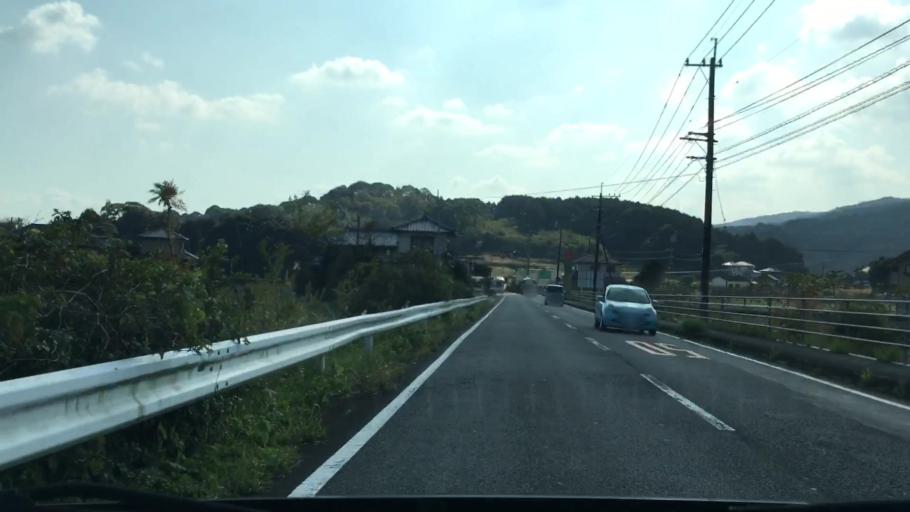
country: JP
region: Nagasaki
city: Togitsu
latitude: 32.9665
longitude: 129.7807
